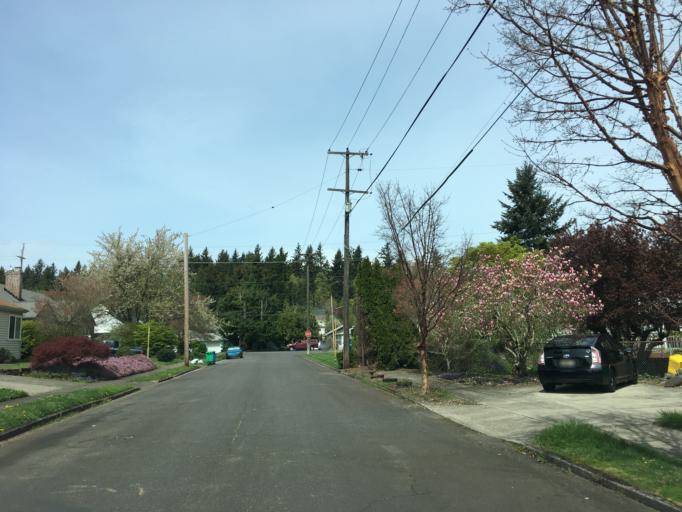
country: US
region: Oregon
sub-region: Multnomah County
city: Lents
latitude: 45.5471
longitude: -122.5710
